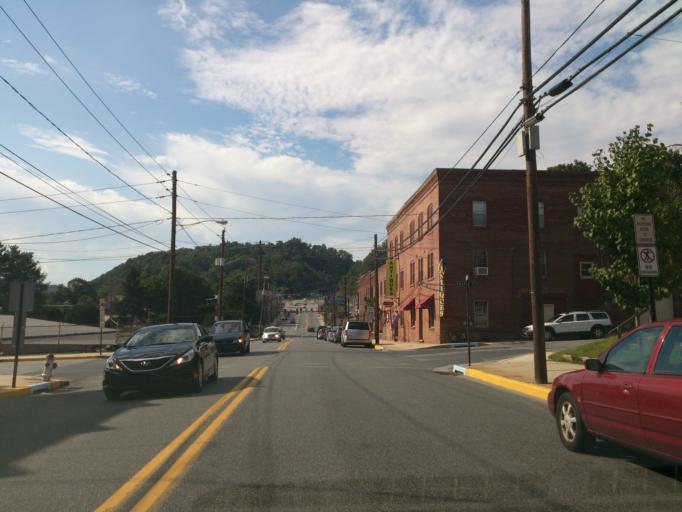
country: US
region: Pennsylvania
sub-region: Lancaster County
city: Columbia
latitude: 40.0357
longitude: -76.5069
